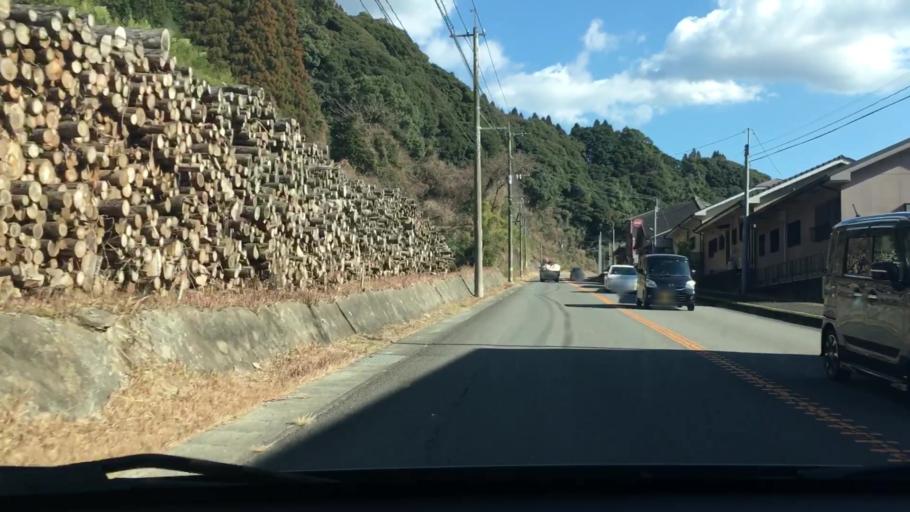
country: JP
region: Kagoshima
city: Satsumasendai
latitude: 31.7987
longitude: 130.4166
